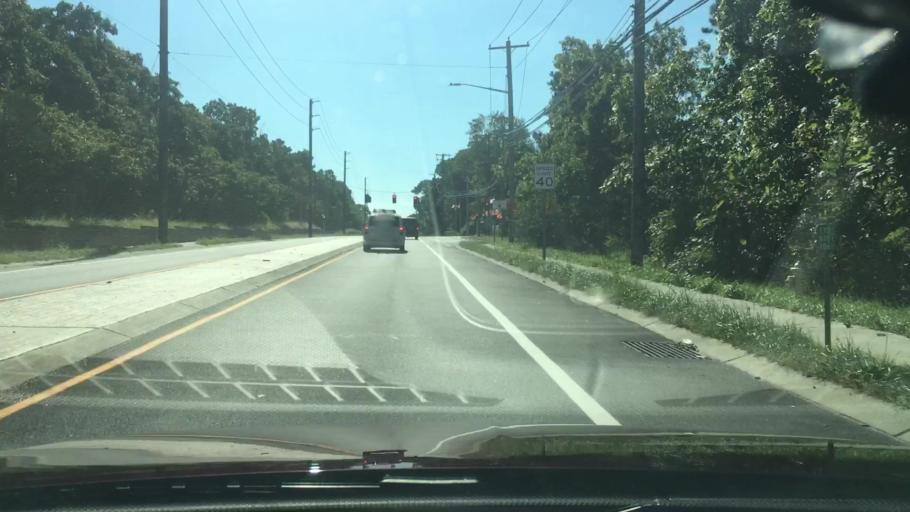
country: US
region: New York
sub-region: Suffolk County
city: Coram
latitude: 40.8579
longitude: -72.9985
